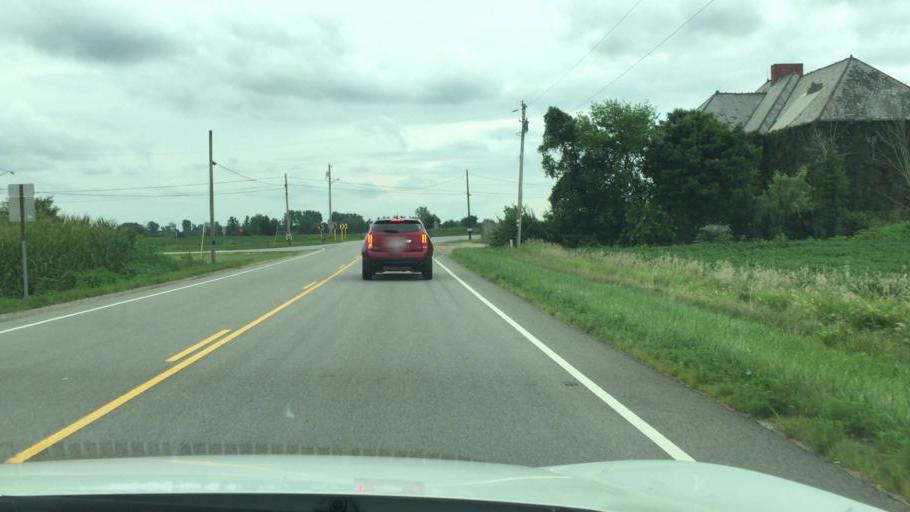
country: US
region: Ohio
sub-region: Champaign County
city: Mechanicsburg
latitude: 40.1254
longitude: -83.4918
